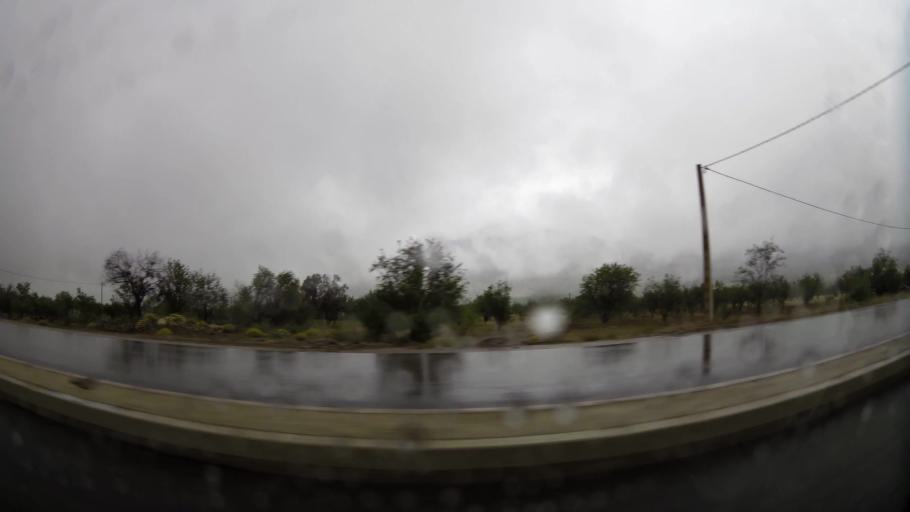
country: MA
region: Oriental
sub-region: Nador
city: Midar
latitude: 34.8444
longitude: -3.7213
